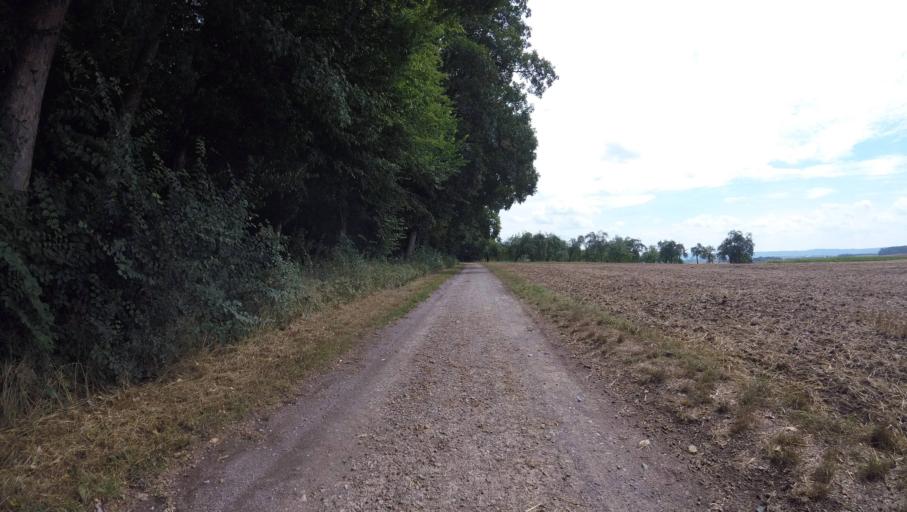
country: DE
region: Baden-Wuerttemberg
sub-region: Regierungsbezirk Stuttgart
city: Kirchberg an der Murr
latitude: 48.9667
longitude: 9.3591
